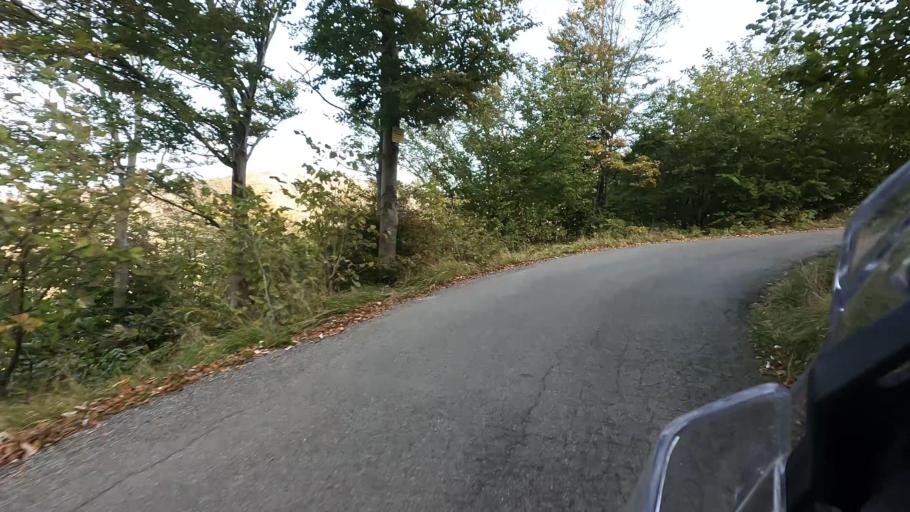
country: IT
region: Liguria
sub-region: Provincia di Genova
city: Sciarborasca
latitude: 44.4376
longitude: 8.5848
